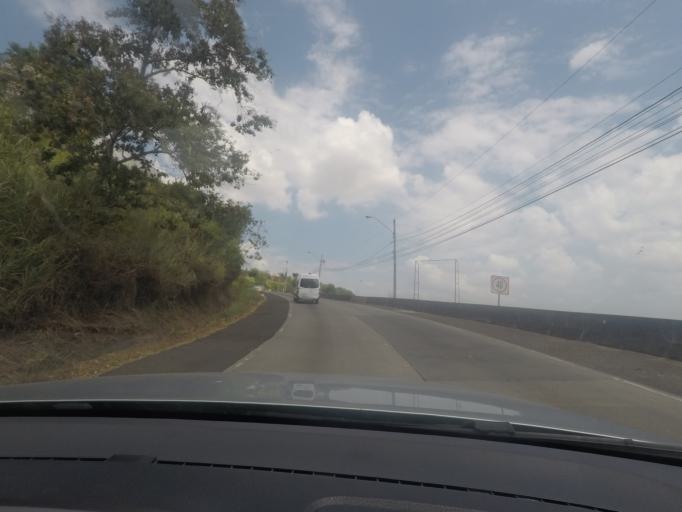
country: PA
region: Panama
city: La Chorrera
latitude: 8.8877
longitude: -79.7698
